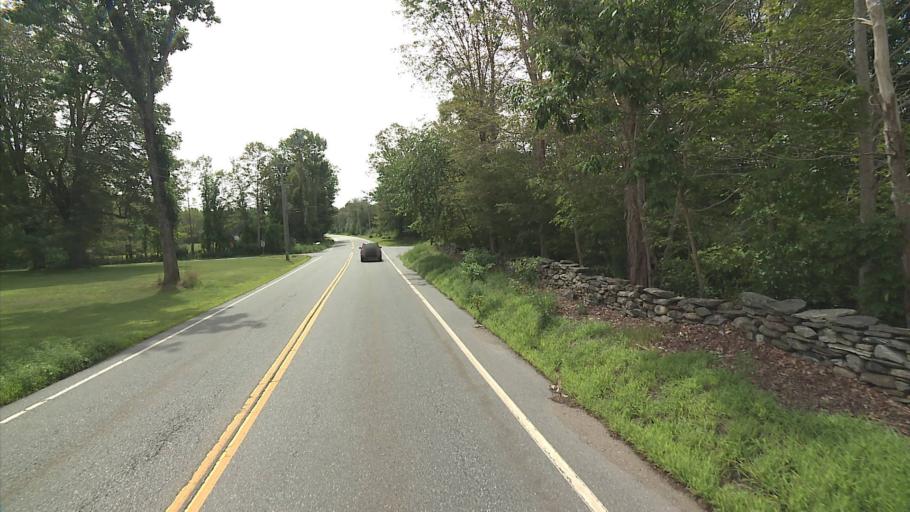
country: US
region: Connecticut
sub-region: Windham County
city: Putnam
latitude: 41.9141
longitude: -71.8713
